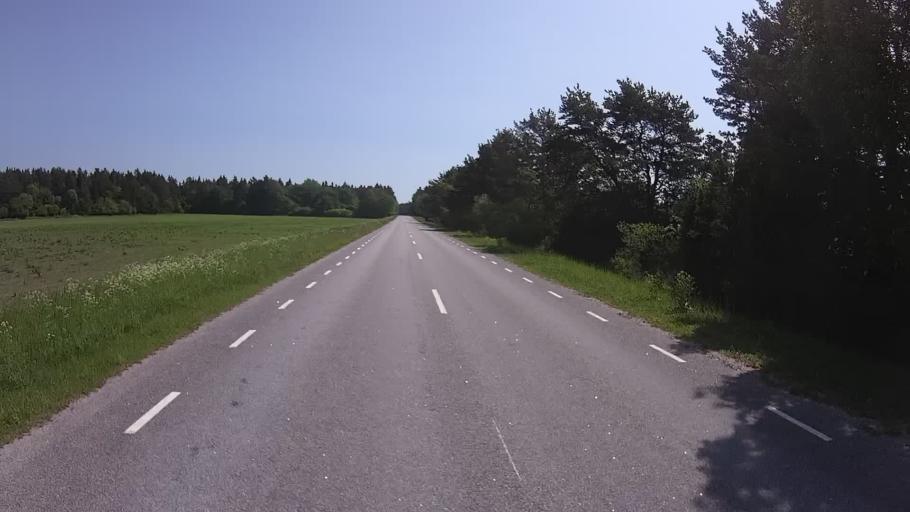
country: EE
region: Saare
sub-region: Kuressaare linn
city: Kuressaare
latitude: 58.3596
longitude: 22.0629
